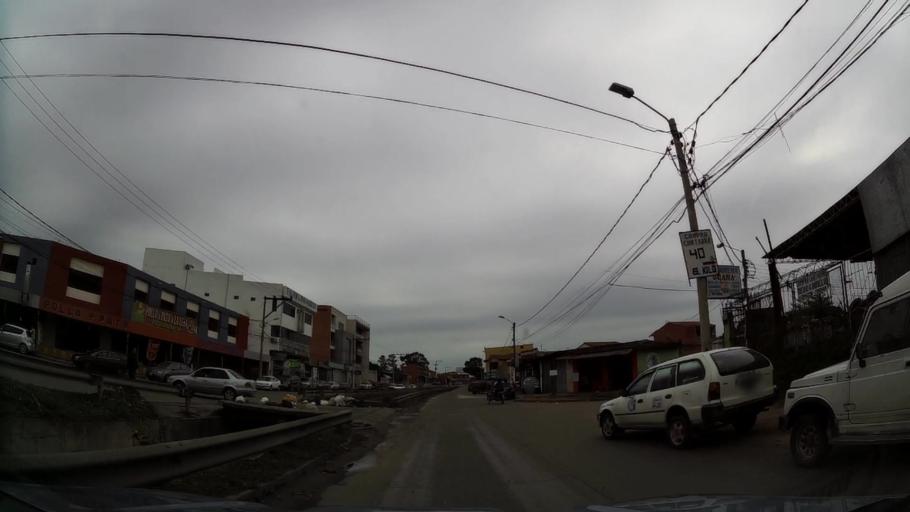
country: BO
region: Santa Cruz
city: Santa Cruz de la Sierra
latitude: -17.8293
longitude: -63.1725
